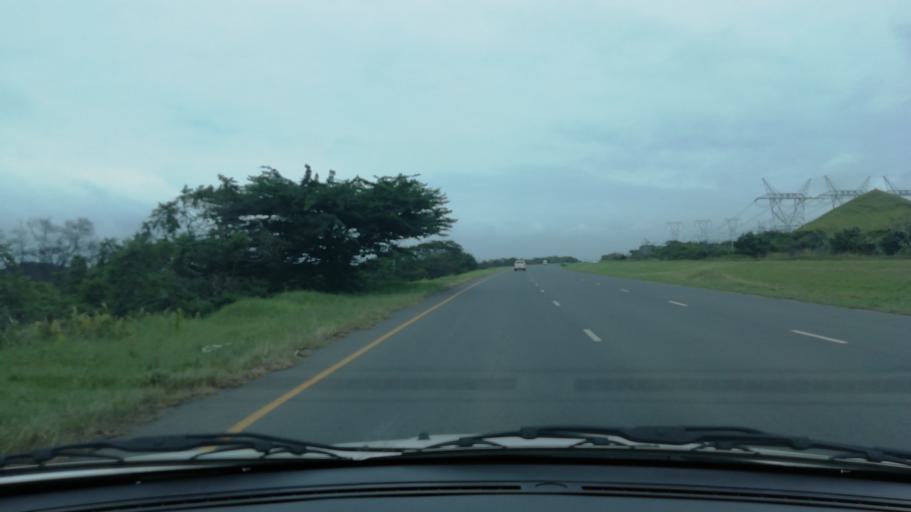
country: ZA
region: KwaZulu-Natal
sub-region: uThungulu District Municipality
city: Richards Bay
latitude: -28.7718
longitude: 32.0274
